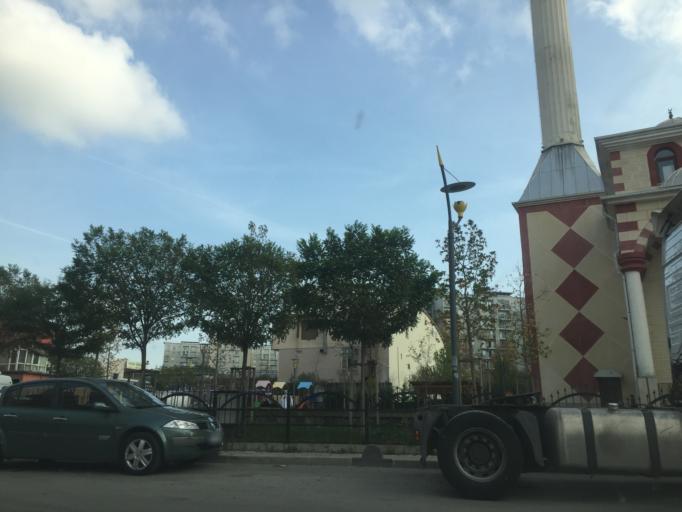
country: TR
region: Istanbul
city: Sultanbeyli
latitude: 40.9422
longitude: 29.3001
